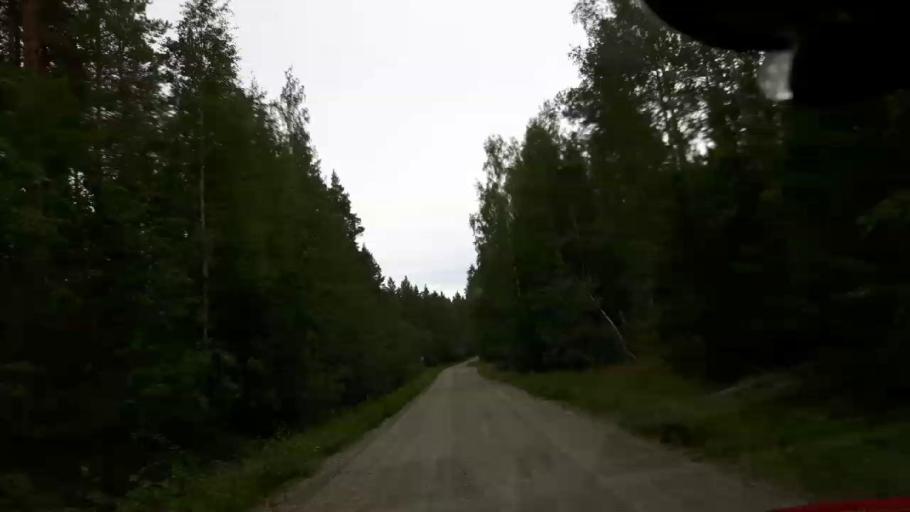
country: SE
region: Vaesternorrland
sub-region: Ange Kommun
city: Ange
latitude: 62.7930
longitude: 15.7728
